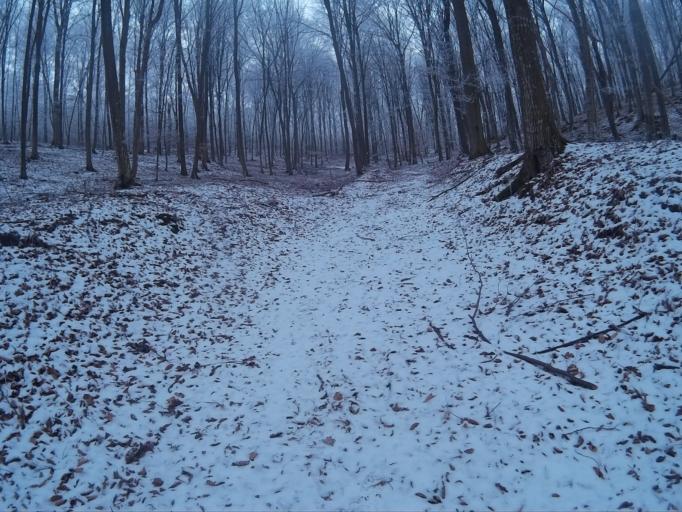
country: HU
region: Borsod-Abauj-Zemplen
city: Szendro
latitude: 48.5548
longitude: 20.6817
